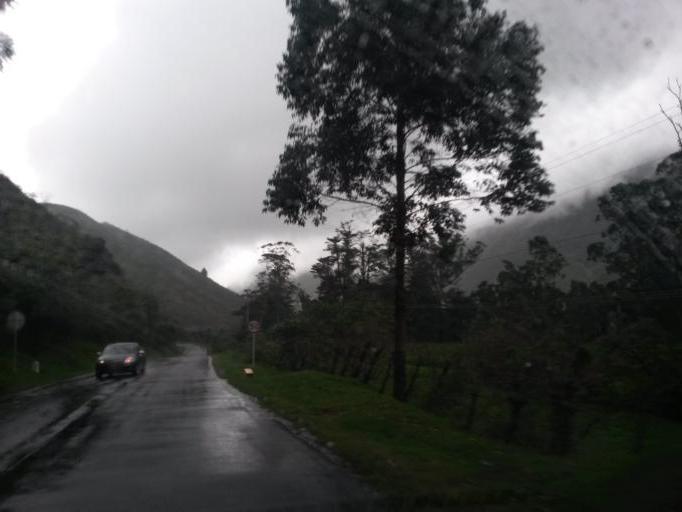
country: CO
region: Cauca
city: Popayan
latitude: 2.3569
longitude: -76.4972
